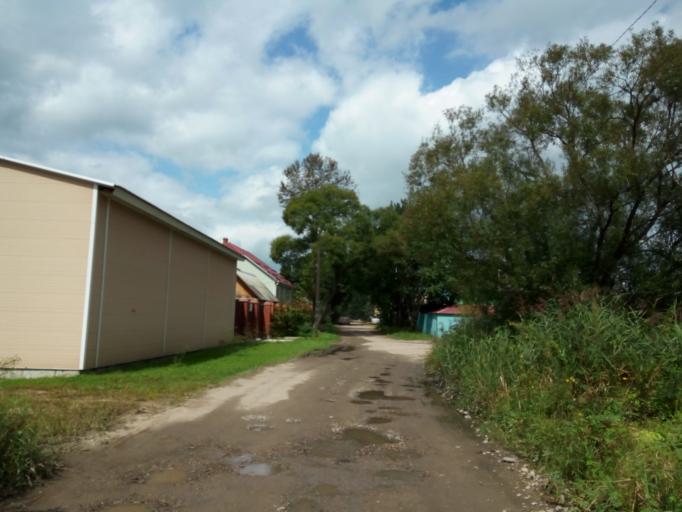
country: RU
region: Primorskiy
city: Dal'nerechensk
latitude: 45.9367
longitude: 133.8107
